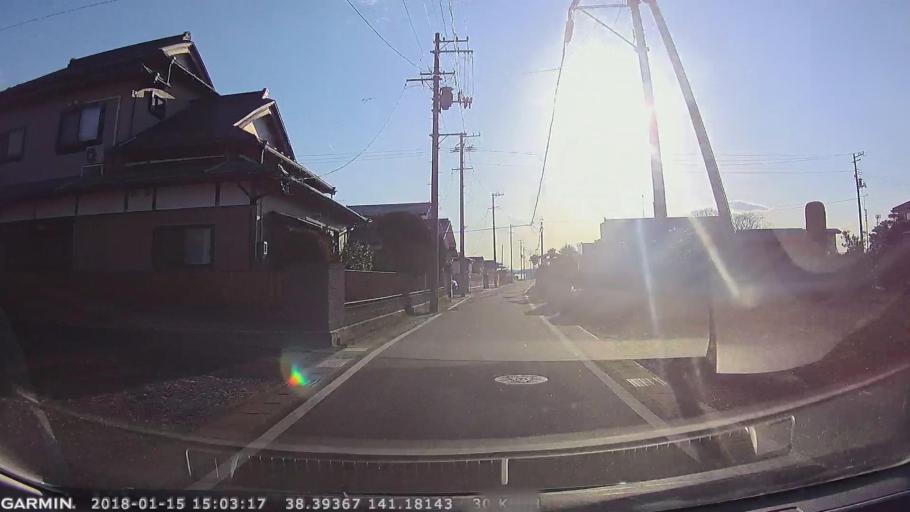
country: JP
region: Miyagi
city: Yamoto
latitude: 38.3939
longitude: 141.1814
